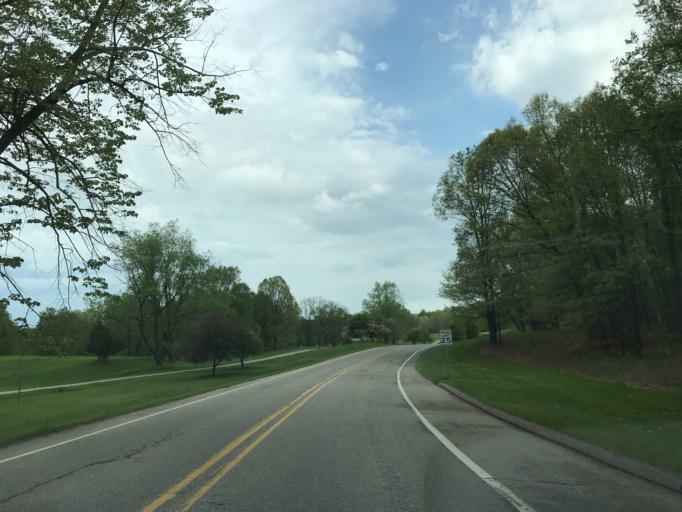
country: US
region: Michigan
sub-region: Oakland County
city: Milford
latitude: 42.5482
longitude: -83.6403
